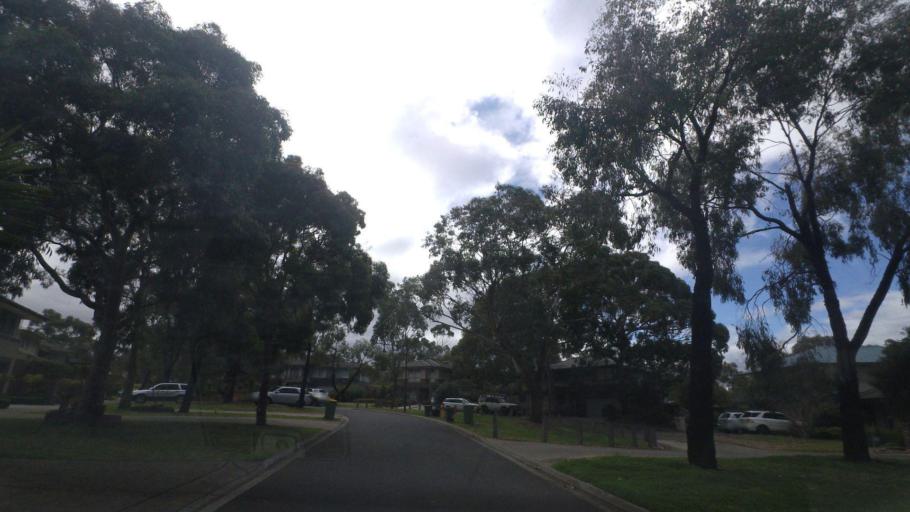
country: AU
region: Victoria
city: Macleod
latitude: -37.7187
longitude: 145.0643
